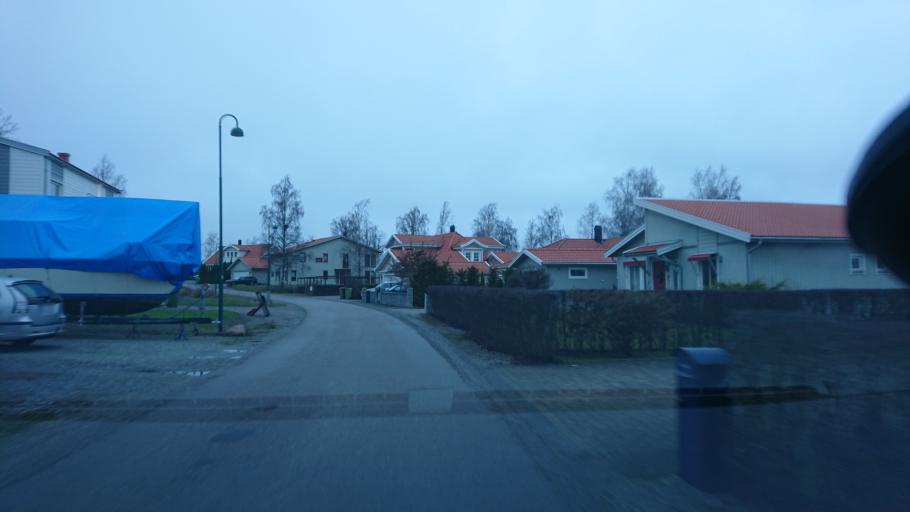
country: SE
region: Soedermanland
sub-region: Strangnas Kommun
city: Stallarholmen
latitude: 59.3630
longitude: 17.1982
